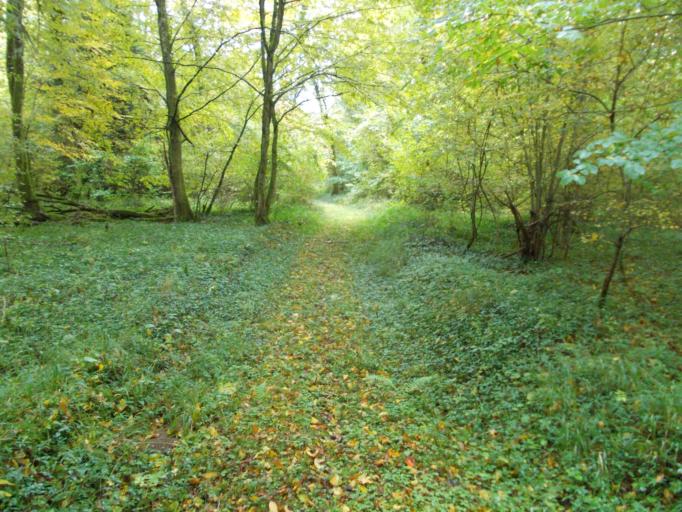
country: FR
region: Lorraine
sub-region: Departement de la Meuse
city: Gondrecourt-le-Chateau
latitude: 48.5625
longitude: 5.3892
